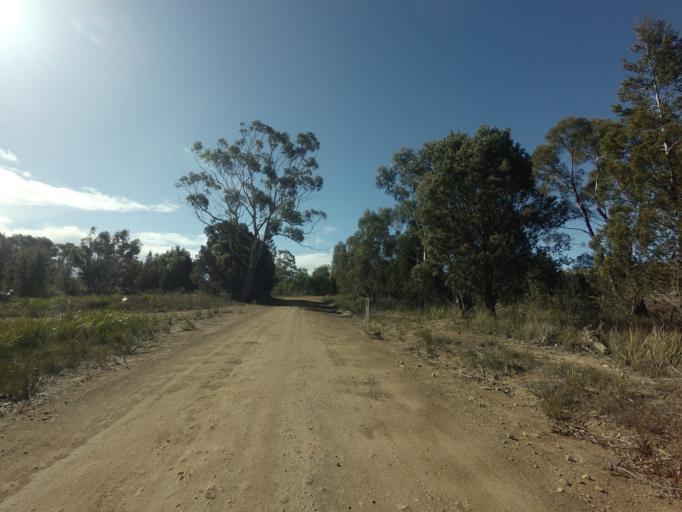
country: AU
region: Tasmania
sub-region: Sorell
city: Sorell
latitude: -42.3529
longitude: 147.9683
